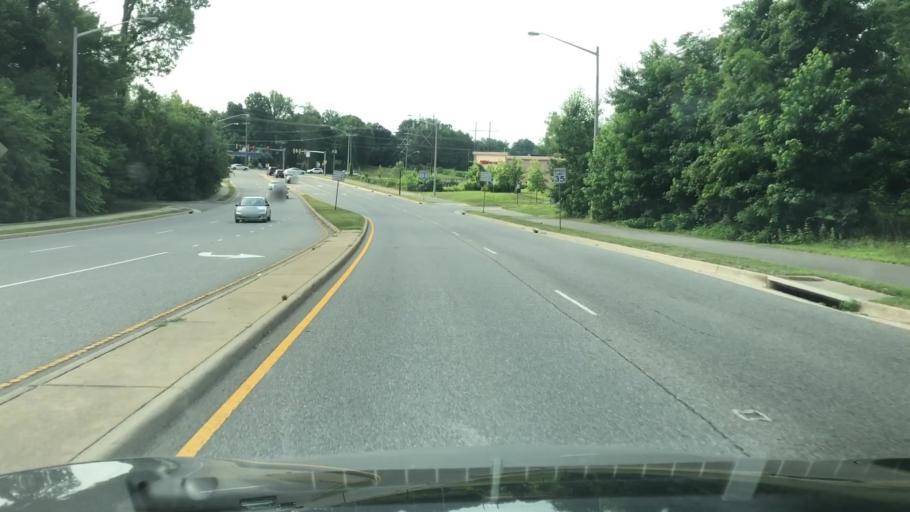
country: US
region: Virginia
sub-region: City of Fredericksburg
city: Fredericksburg
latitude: 38.3021
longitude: -77.4839
